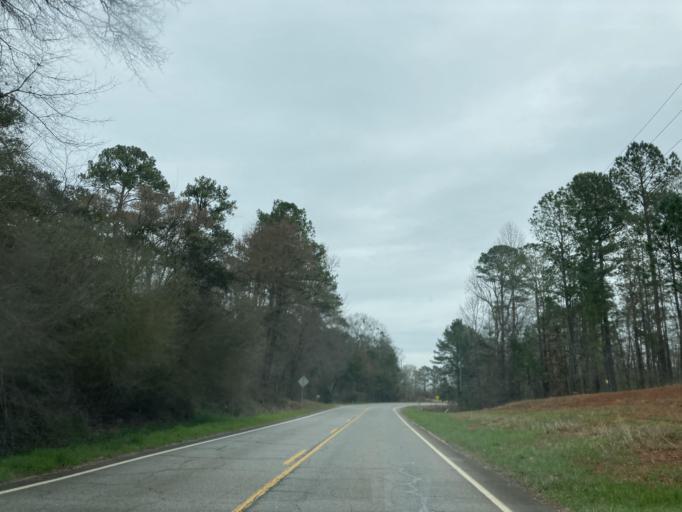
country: US
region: Georgia
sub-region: Jones County
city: Gray
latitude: 32.9732
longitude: -83.6282
